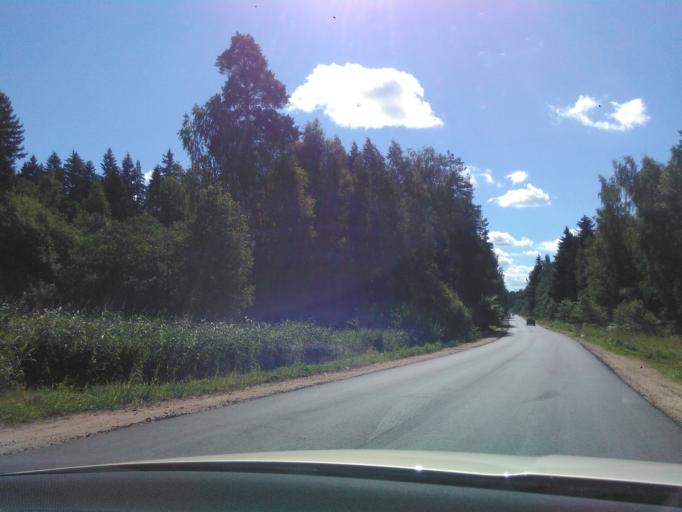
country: RU
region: Moskovskaya
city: Klin
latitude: 56.2411
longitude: 36.8319
